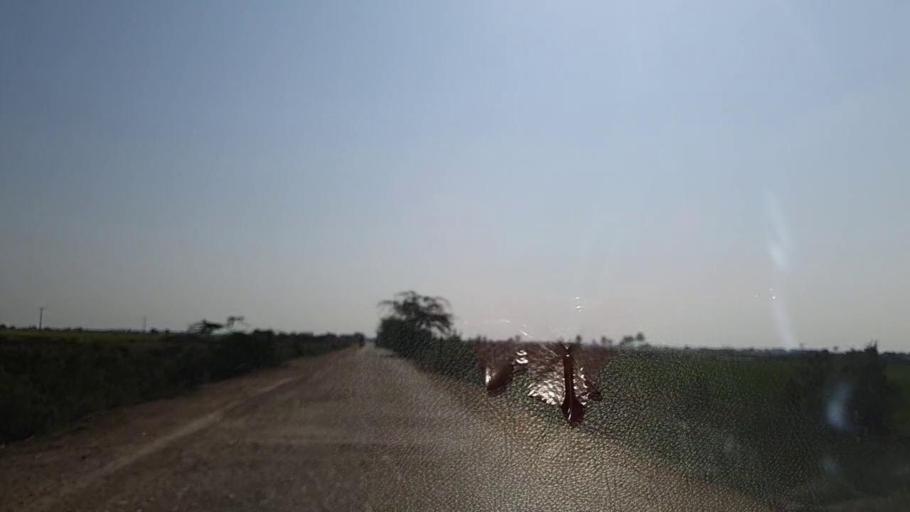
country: PK
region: Sindh
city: Sanghar
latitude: 25.9937
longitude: 69.0605
